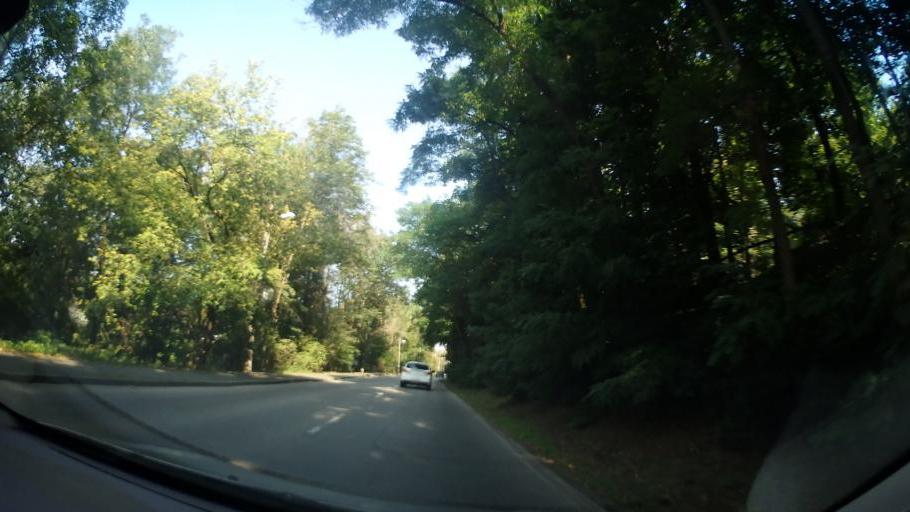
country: CZ
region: South Moravian
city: Troubsko
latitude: 49.2298
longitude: 16.5323
